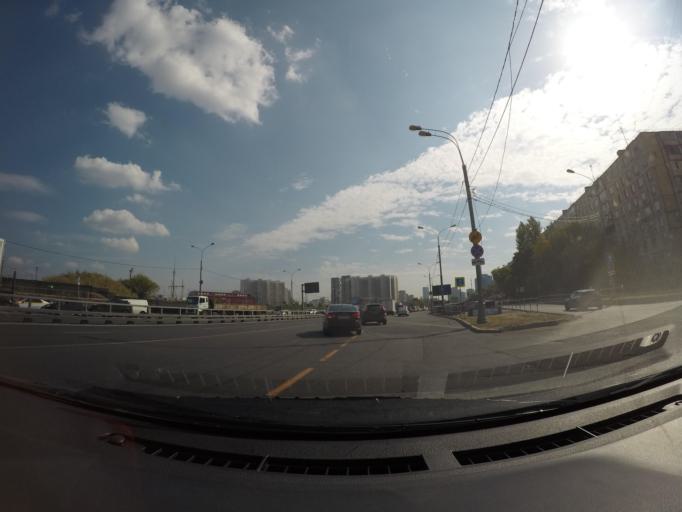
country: RU
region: Moscow
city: Likhobory
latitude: 55.8350
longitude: 37.5723
